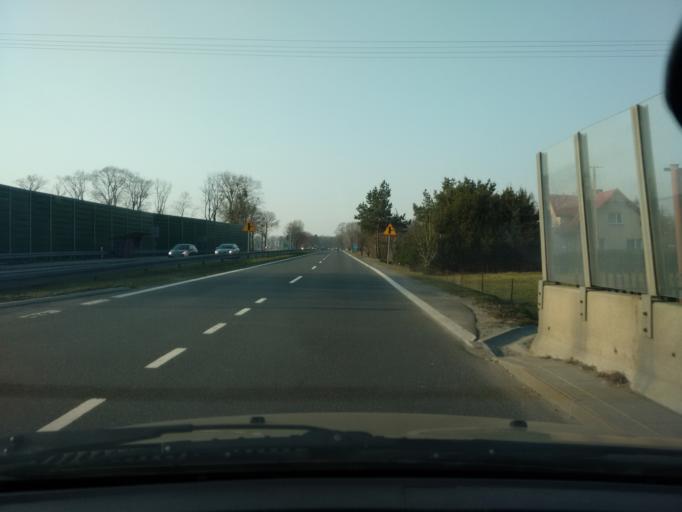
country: PL
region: Silesian Voivodeship
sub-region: Powiat cieszynski
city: Ochaby
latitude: 49.8524
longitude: 18.7607
